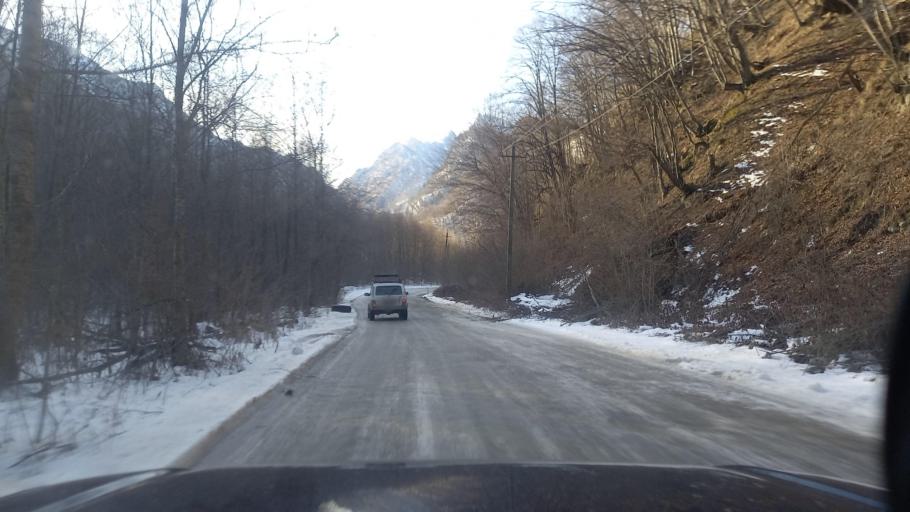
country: RU
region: North Ossetia
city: Gizel'
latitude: 42.9160
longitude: 44.5364
